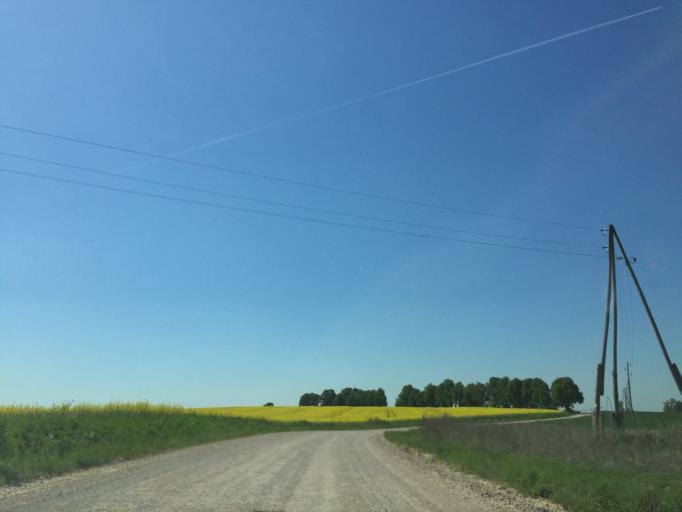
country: LV
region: Rundales
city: Pilsrundale
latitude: 56.4903
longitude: 24.0806
